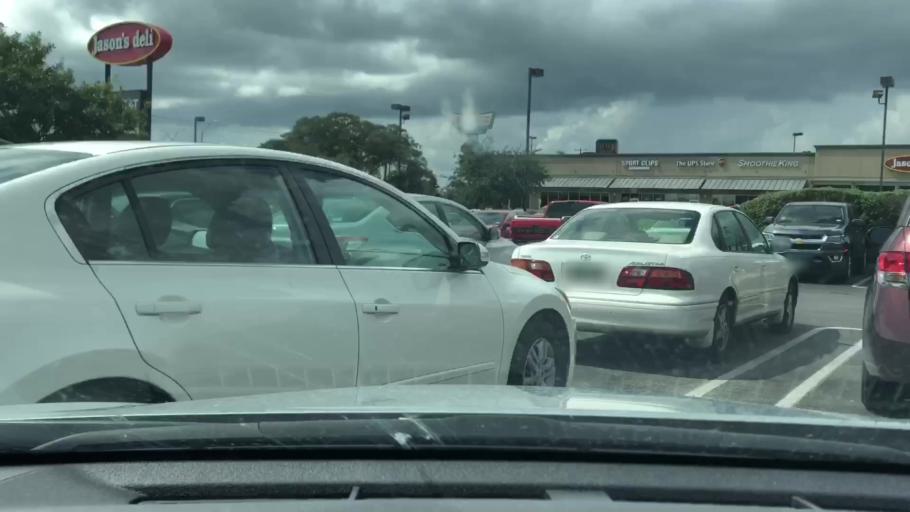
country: US
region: Texas
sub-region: Bexar County
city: Hollywood Park
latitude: 29.6114
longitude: -98.4755
